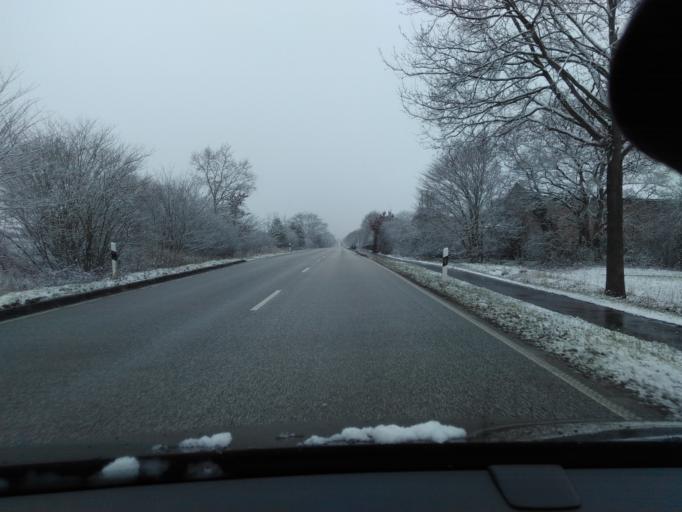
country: DE
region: Schleswig-Holstein
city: Ahrensbok
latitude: 54.0360
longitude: 10.6170
